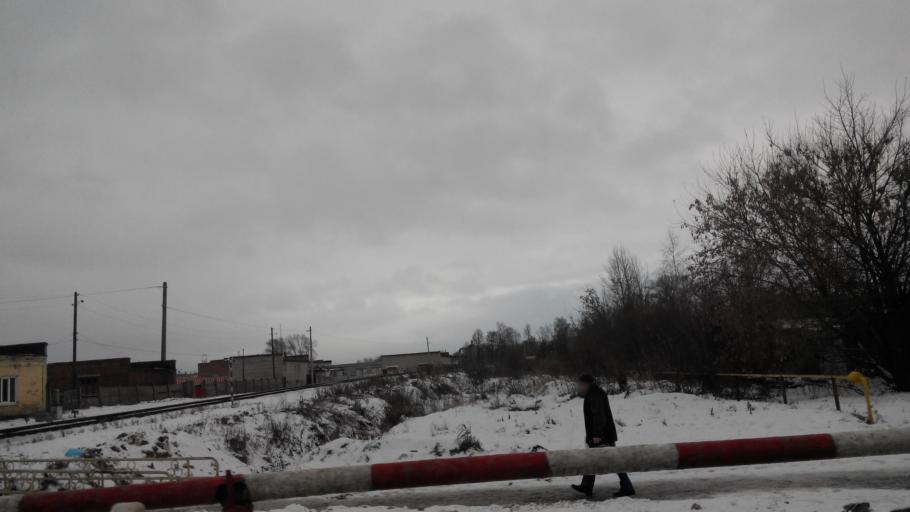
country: RU
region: Tula
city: Uzlovaya
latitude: 53.9723
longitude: 38.1773
